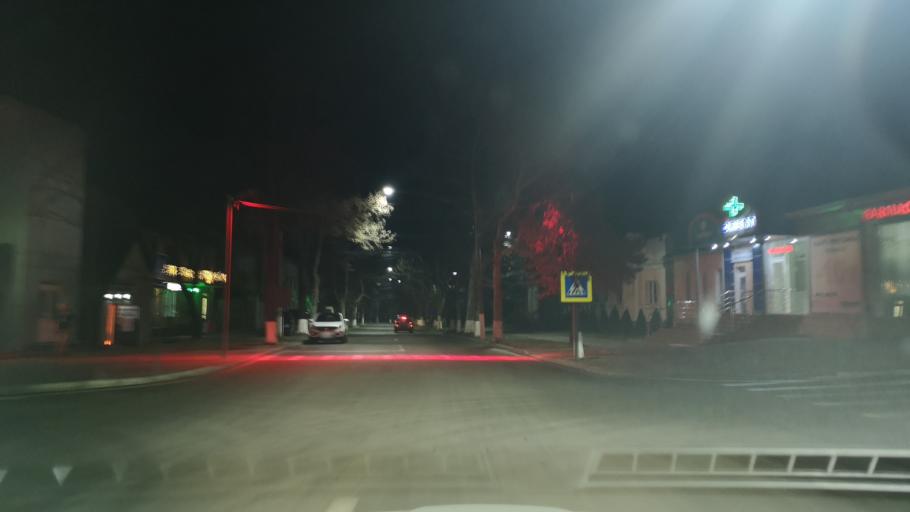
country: MD
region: Orhei
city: Orhei
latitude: 47.3866
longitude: 28.8247
